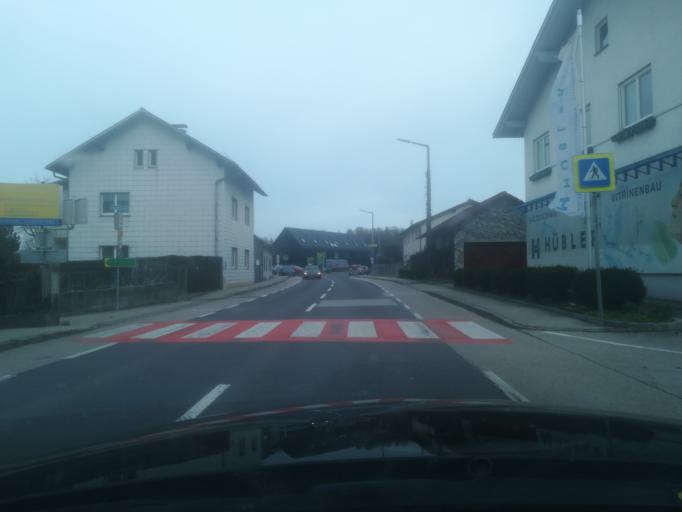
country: AT
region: Upper Austria
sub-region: Wels-Land
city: Thalheim bei Wels
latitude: 48.1533
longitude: 14.0388
